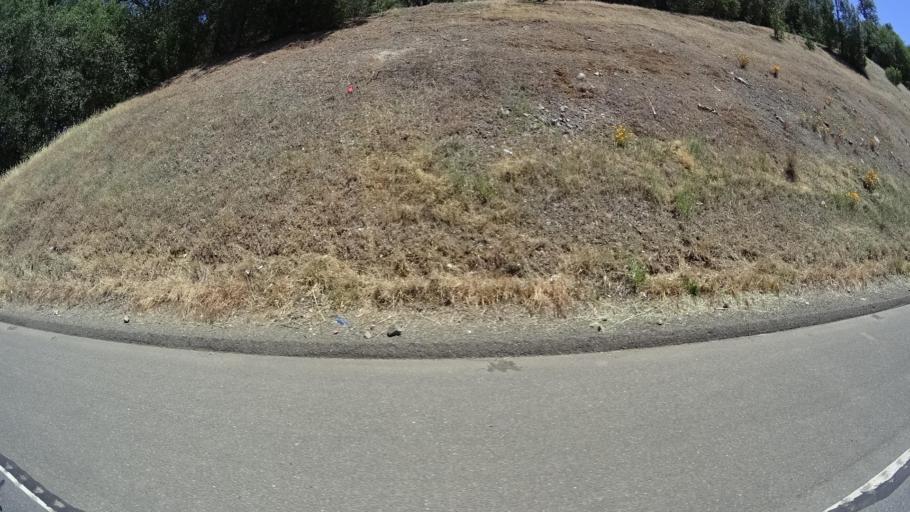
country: US
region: California
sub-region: Lake County
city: Clearlake
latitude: 38.9411
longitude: -122.6234
